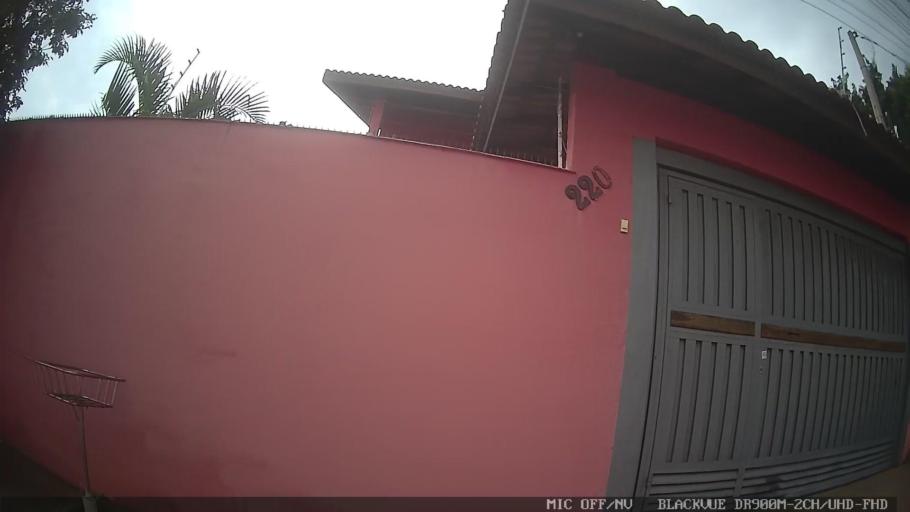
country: BR
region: Sao Paulo
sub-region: Atibaia
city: Atibaia
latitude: -23.1257
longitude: -46.5918
